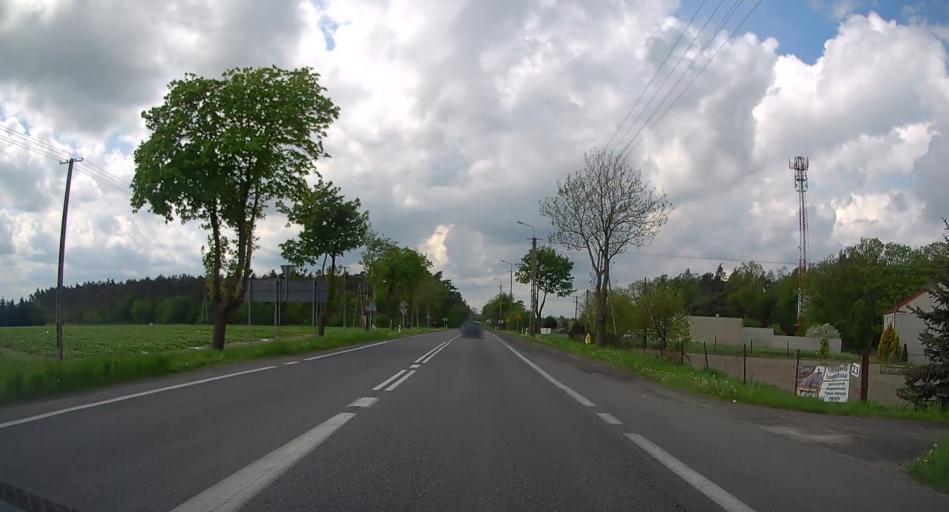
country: PL
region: Masovian Voivodeship
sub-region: Powiat nowodworski
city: Zakroczym
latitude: 52.4476
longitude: 20.5858
